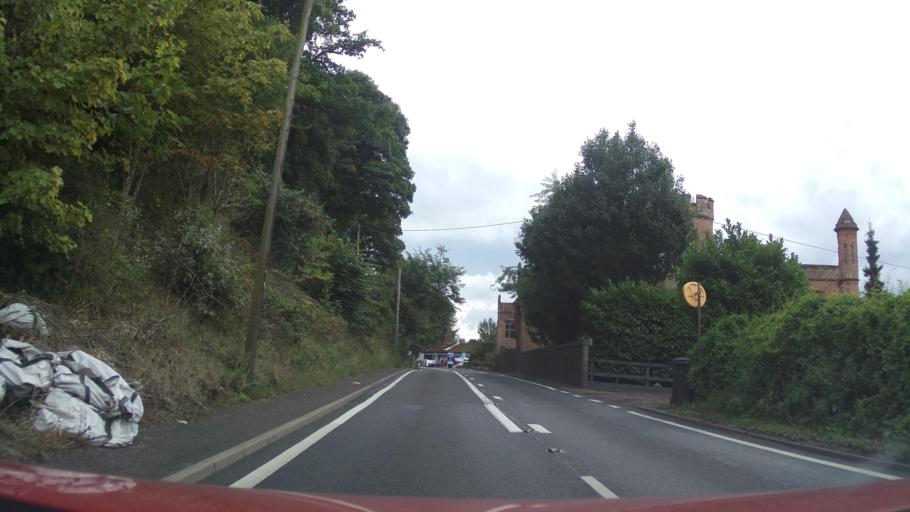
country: GB
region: England
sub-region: Shropshire
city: Bridgnorth
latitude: 52.5469
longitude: -2.4079
